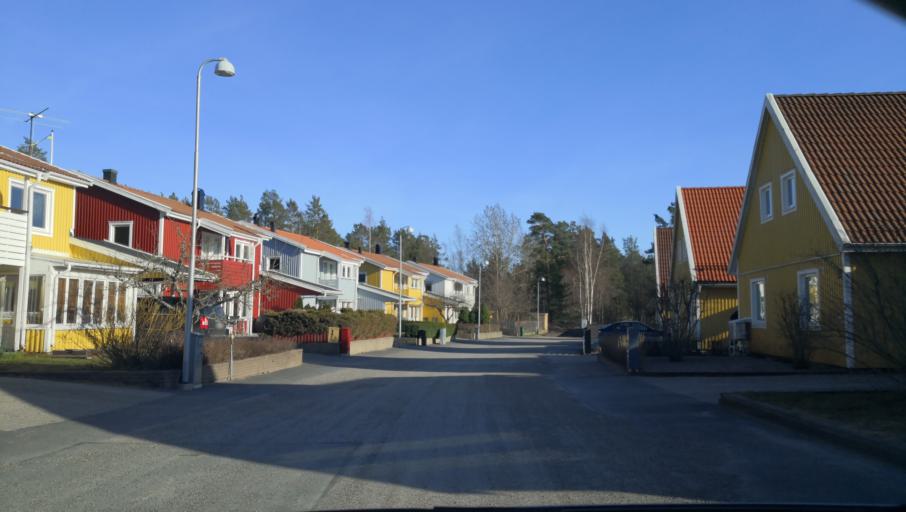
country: SE
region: Stockholm
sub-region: Varmdo Kommun
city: Gustavsberg
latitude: 59.3379
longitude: 18.3787
